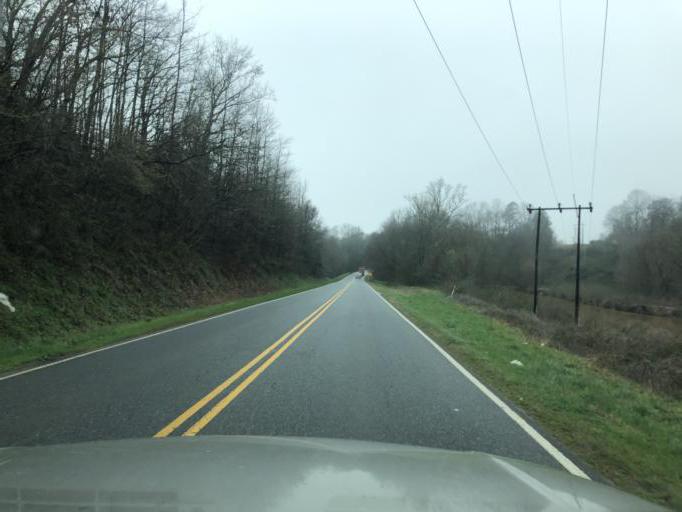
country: US
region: North Carolina
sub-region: Cleveland County
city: Shelby
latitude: 35.3259
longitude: -81.4717
